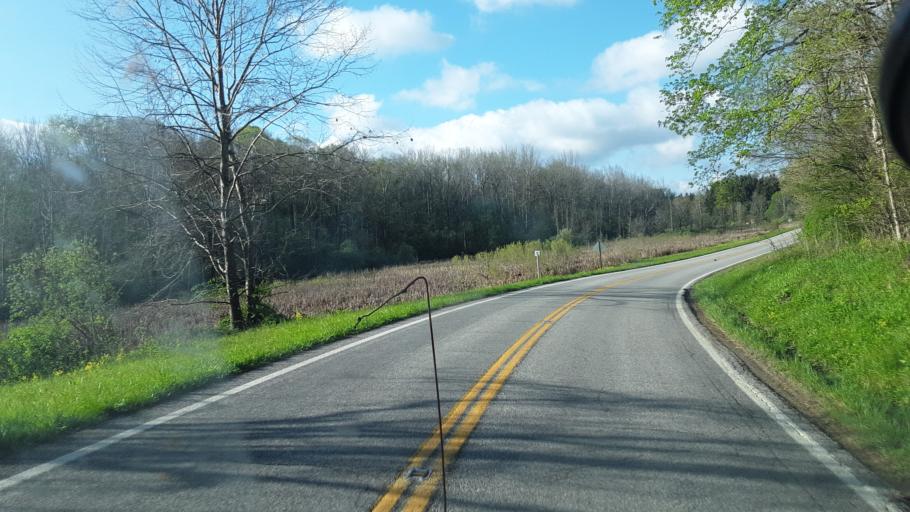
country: US
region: Ohio
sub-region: Noble County
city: Caldwell
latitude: 39.8184
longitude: -81.6710
